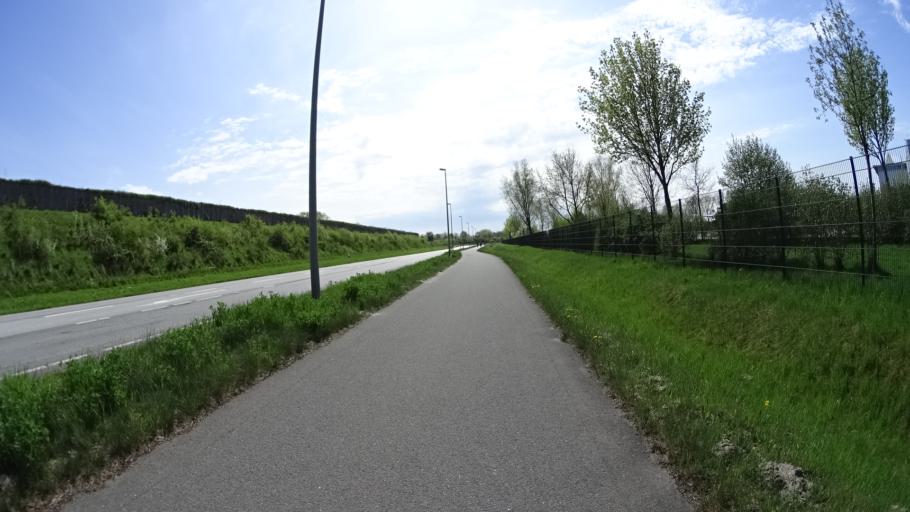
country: DE
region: Lower Saxony
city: Neu Wulmstorf
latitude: 53.5336
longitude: 9.8429
